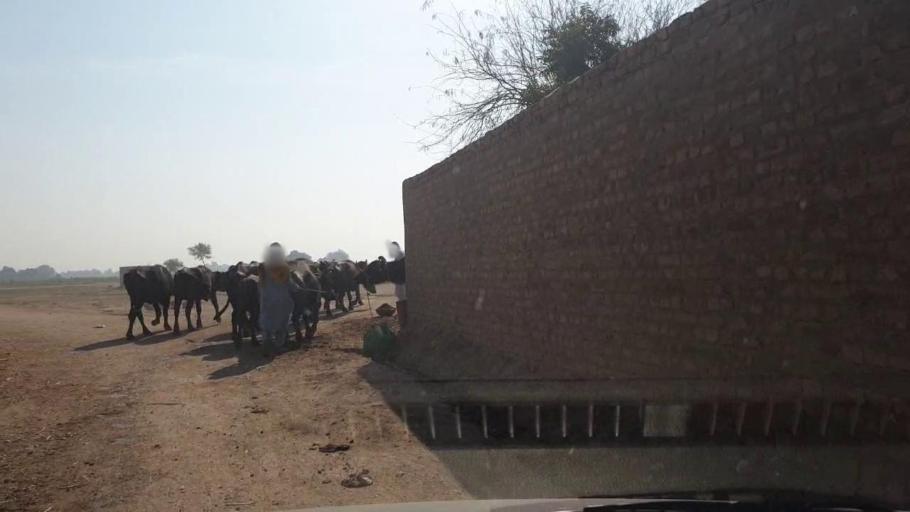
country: PK
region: Sindh
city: Tando Allahyar
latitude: 25.4054
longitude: 68.7376
